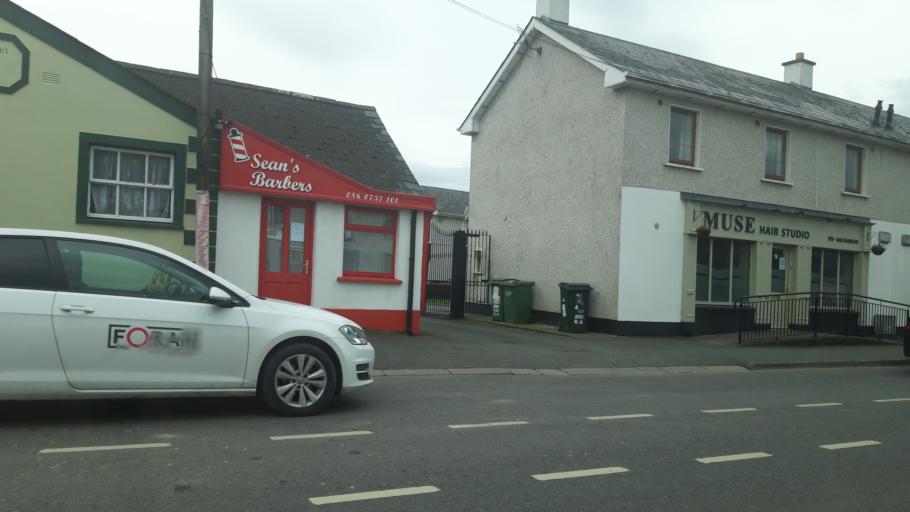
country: IE
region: Leinster
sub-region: Kildare
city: Prosperous
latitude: 53.2915
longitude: -6.7542
